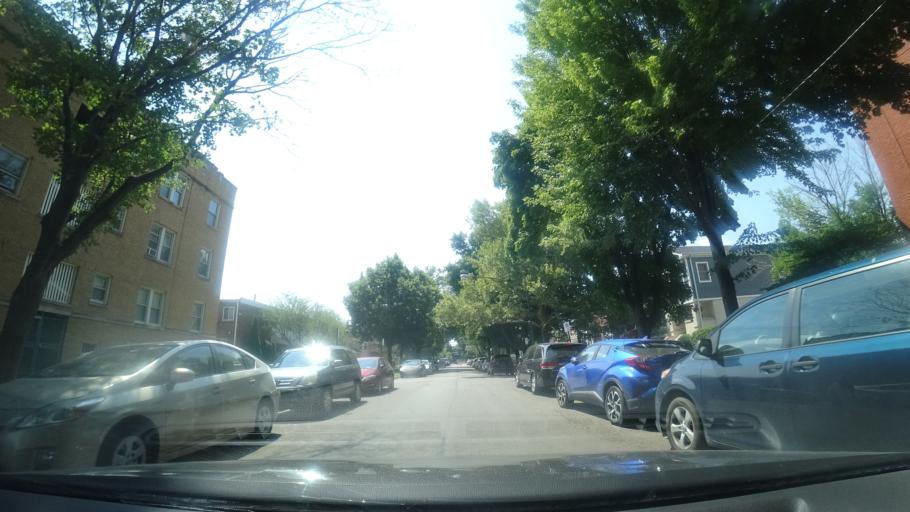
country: US
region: Illinois
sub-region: Cook County
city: Evanston
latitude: 41.9881
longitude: -87.6731
